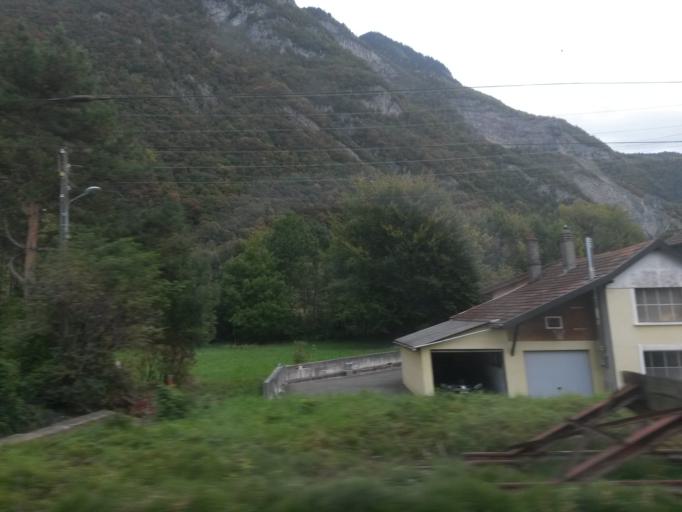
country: CH
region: Vaud
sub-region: Aigle District
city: Villeneuve
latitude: 46.3668
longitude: 6.9241
